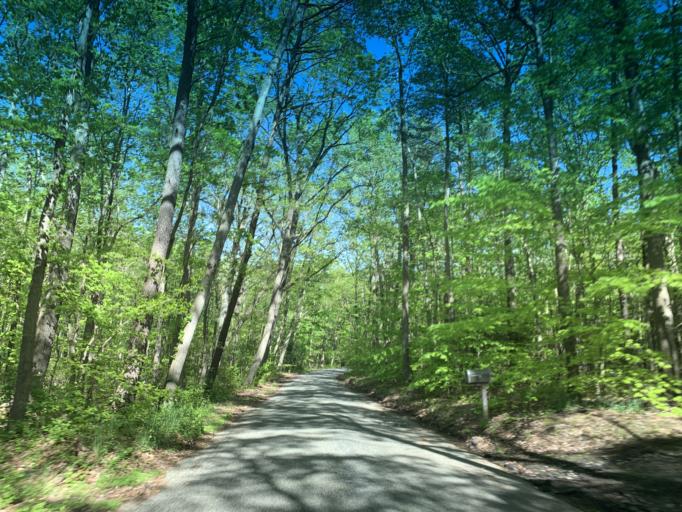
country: US
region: Maryland
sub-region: Harford County
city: Riverside
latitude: 39.4520
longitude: -76.2637
